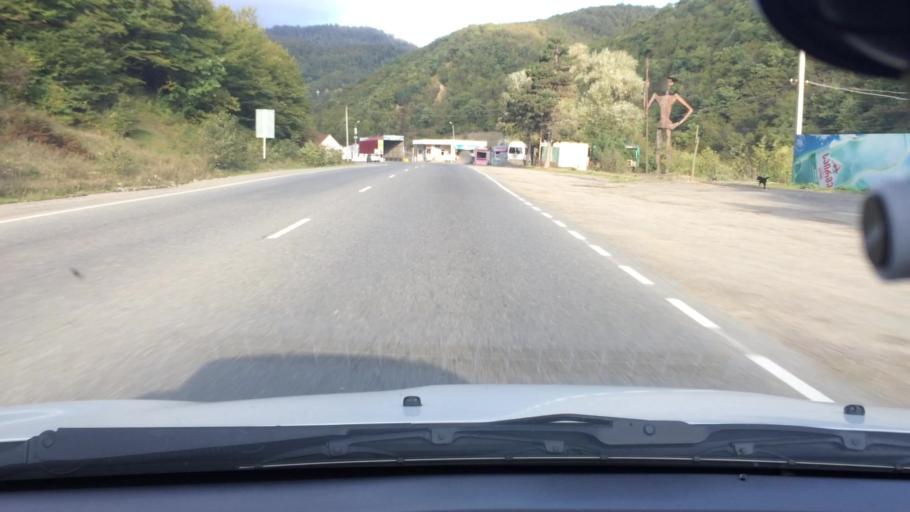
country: GE
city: Surami
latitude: 42.0396
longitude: 43.5118
